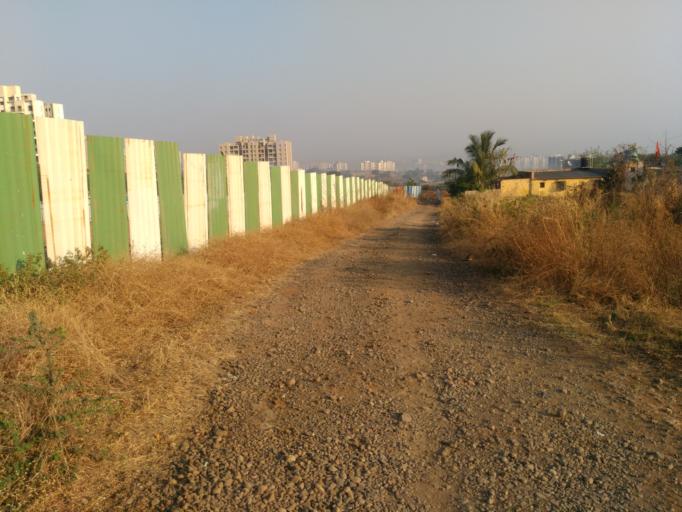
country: IN
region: Maharashtra
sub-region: Pune Division
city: Pune
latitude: 18.4317
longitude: 73.9013
